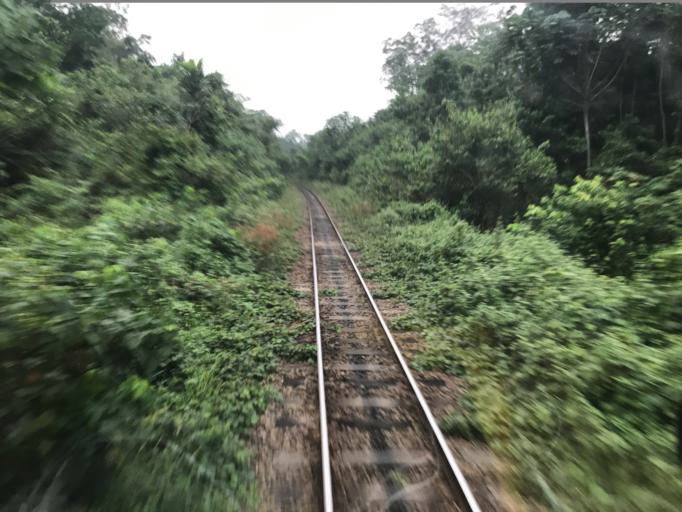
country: CM
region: Littoral
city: Edea
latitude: 3.9828
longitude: 10.0601
